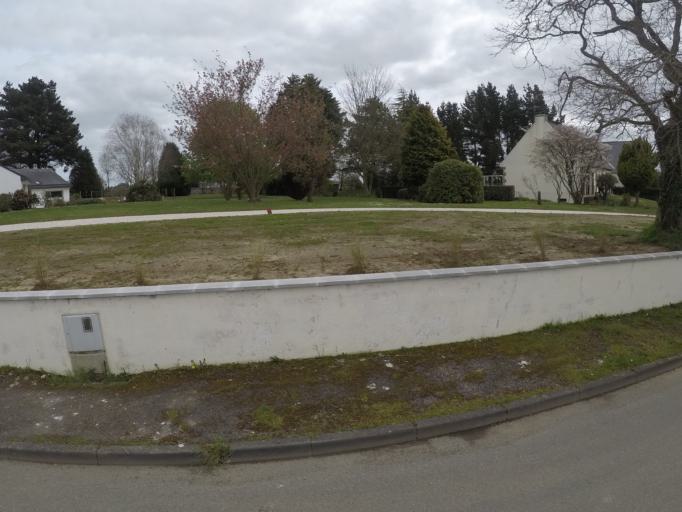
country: FR
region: Brittany
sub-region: Departement des Cotes-d'Armor
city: Plouha
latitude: 48.6803
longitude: -2.9252
